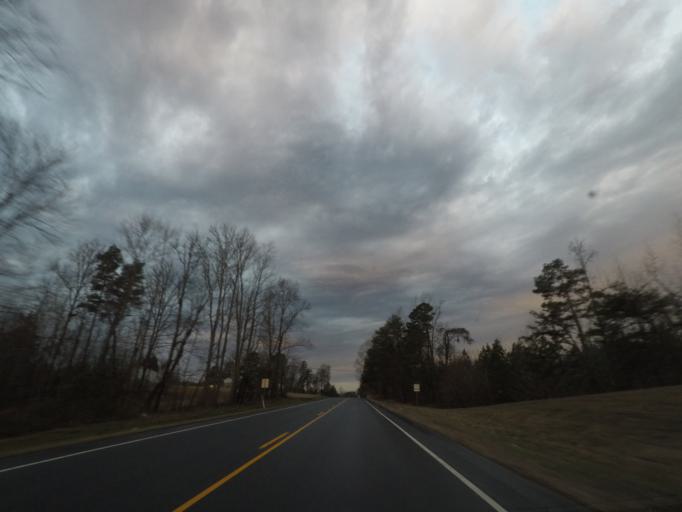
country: US
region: North Carolina
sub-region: Caswell County
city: Yanceyville
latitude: 36.4069
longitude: -79.3092
